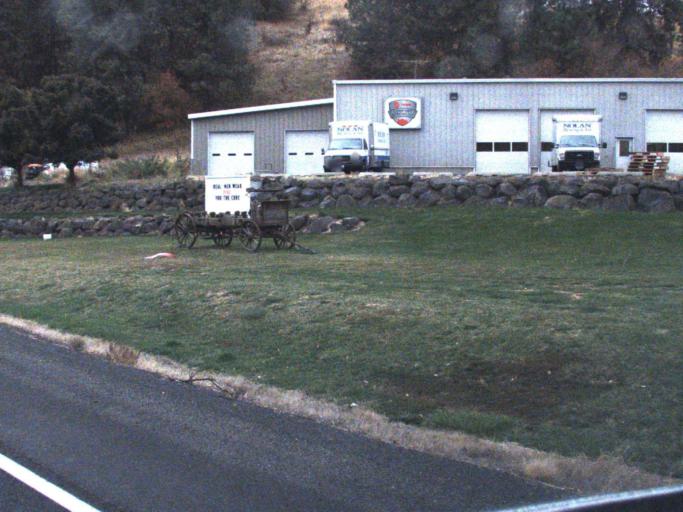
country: US
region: Washington
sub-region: Whitman County
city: Colfax
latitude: 46.8593
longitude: -117.3498
